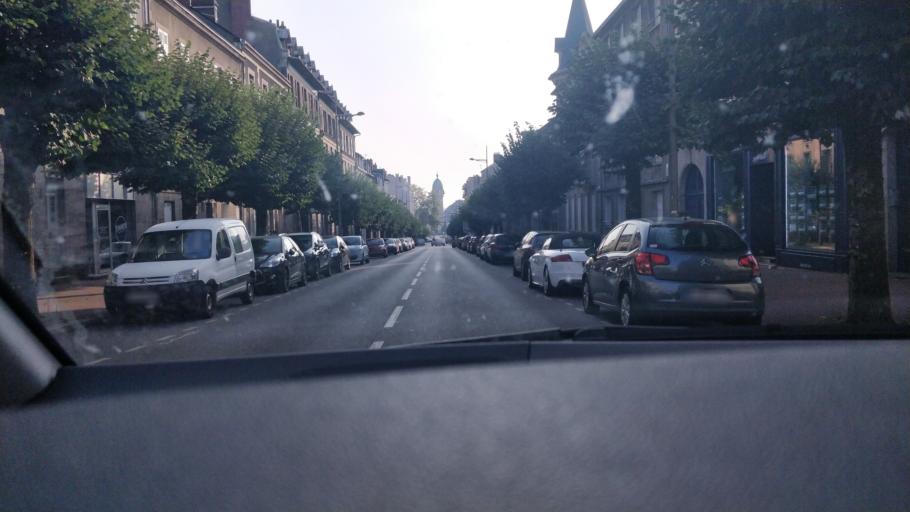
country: FR
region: Limousin
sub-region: Departement de la Haute-Vienne
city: Limoges
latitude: 45.8337
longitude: 1.2583
